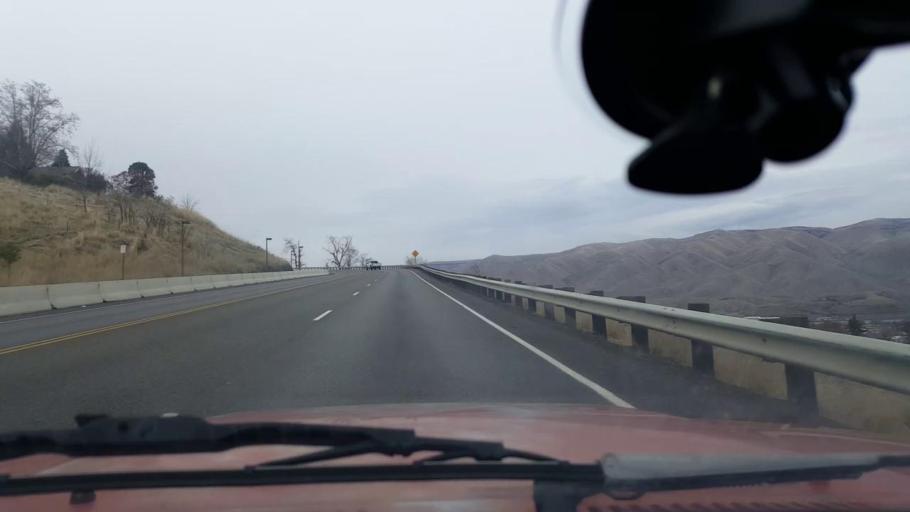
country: US
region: Washington
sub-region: Asotin County
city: West Clarkston-Highland
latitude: 46.4003
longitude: -117.0731
